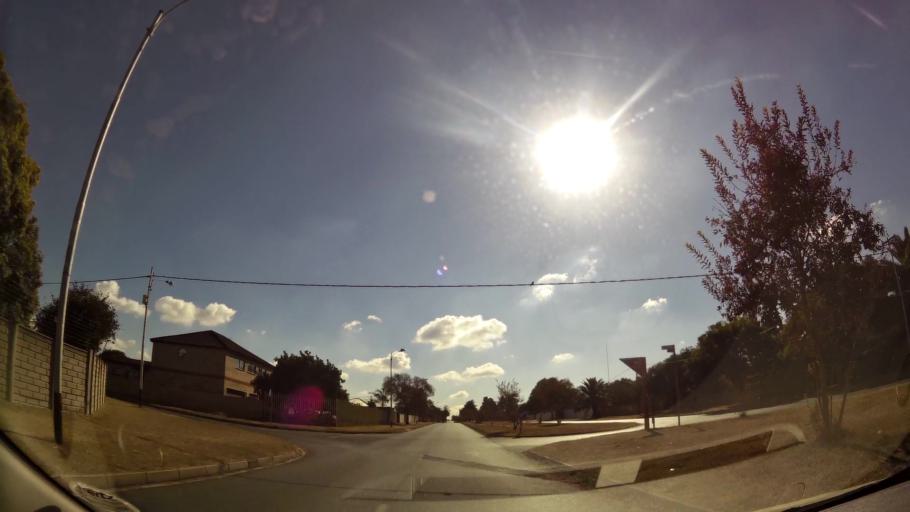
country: ZA
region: Gauteng
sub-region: City of Johannesburg Metropolitan Municipality
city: Roodepoort
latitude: -26.1438
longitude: 27.8347
